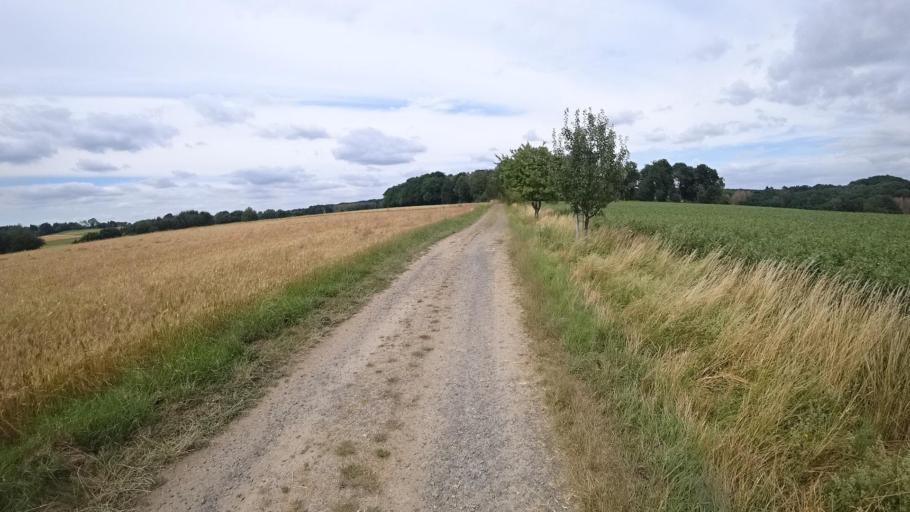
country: DE
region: Rheinland-Pfalz
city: Orfgen
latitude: 50.6715
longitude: 7.5383
